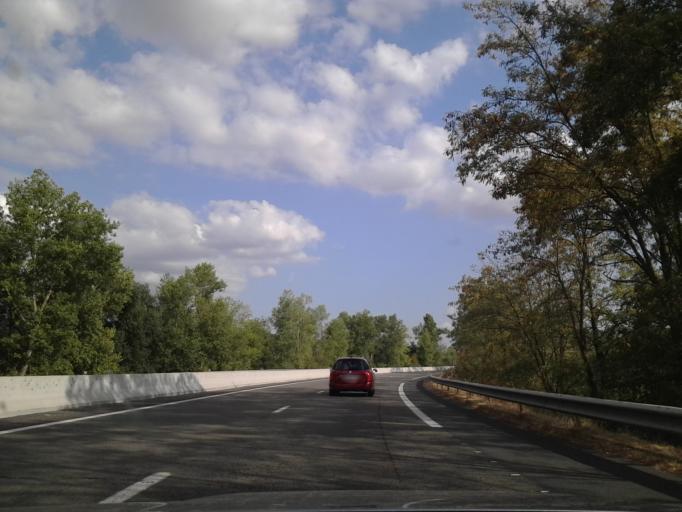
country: FR
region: Auvergne
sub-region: Departement du Puy-de-Dome
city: Issoire
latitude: 45.5608
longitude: 3.2666
